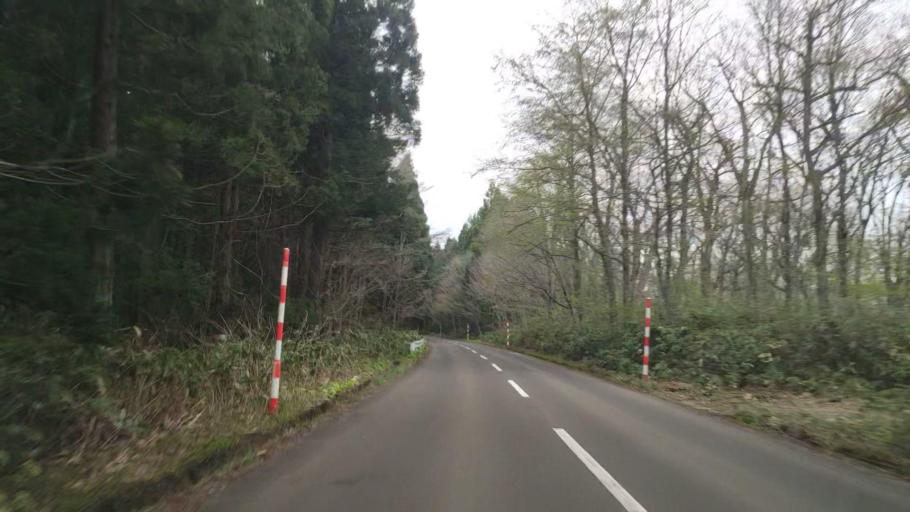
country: JP
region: Akita
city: Hanawa
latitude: 40.3936
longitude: 140.7955
